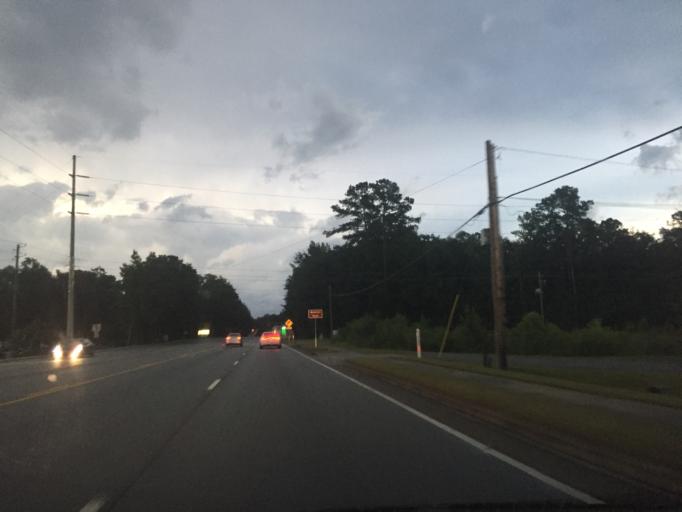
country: US
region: Georgia
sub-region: Liberty County
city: Hinesville
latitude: 31.8580
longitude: -81.5674
